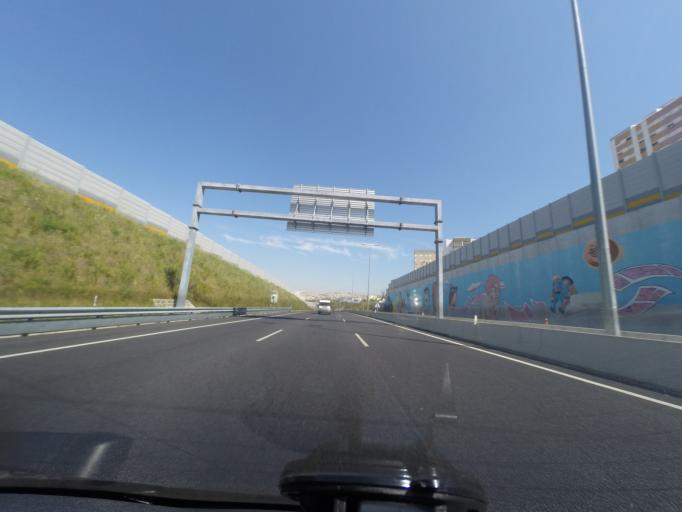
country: PT
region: Lisbon
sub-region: Odivelas
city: Pontinha
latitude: 38.7621
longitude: -9.2021
